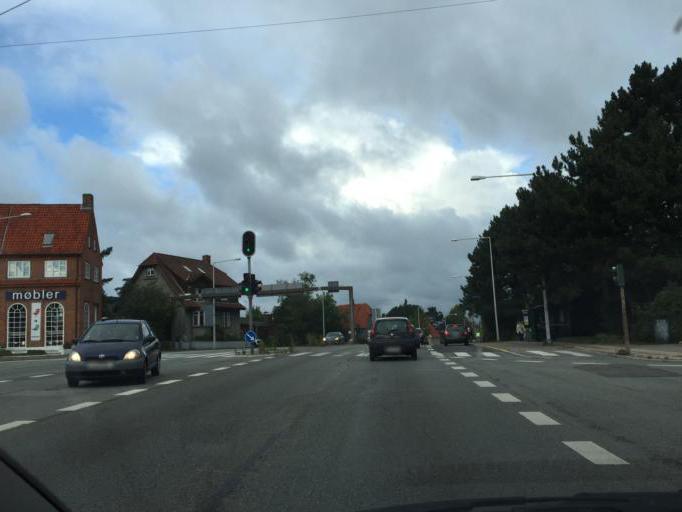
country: DK
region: Capital Region
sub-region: Kobenhavn
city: Vanlose
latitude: 55.7092
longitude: 12.5093
